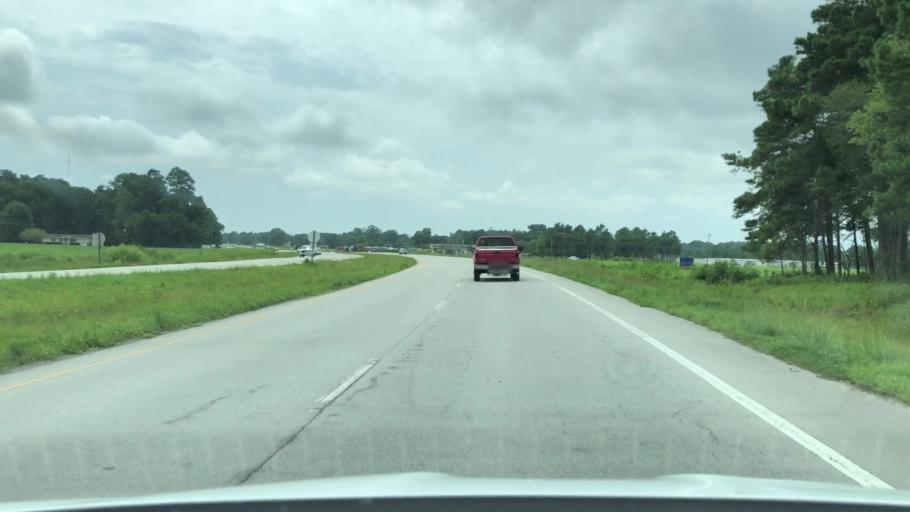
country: US
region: North Carolina
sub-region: Carteret County
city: Newport
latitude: 34.8148
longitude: -76.8796
